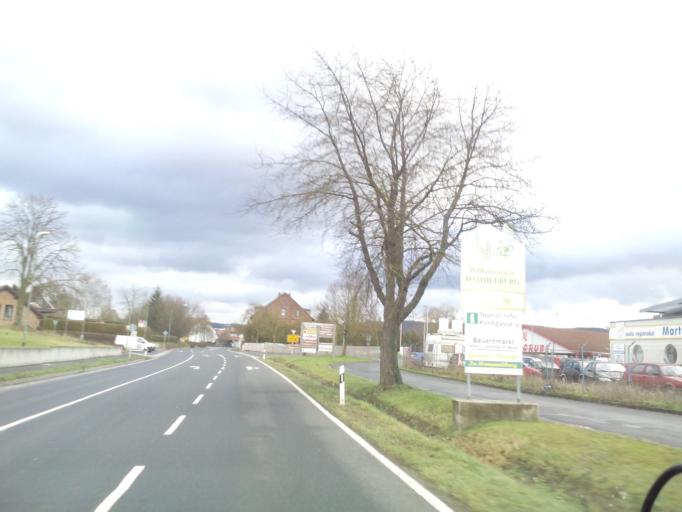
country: DE
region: Bavaria
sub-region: Regierungsbezirk Unterfranken
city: Hammelburg
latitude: 50.1189
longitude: 9.8804
